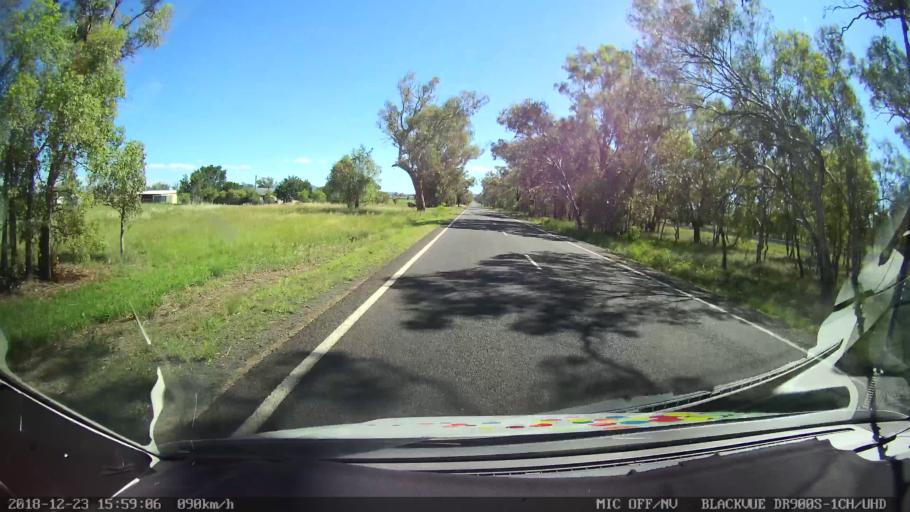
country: AU
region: New South Wales
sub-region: Tamworth Municipality
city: Phillip
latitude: -31.1958
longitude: 150.8361
